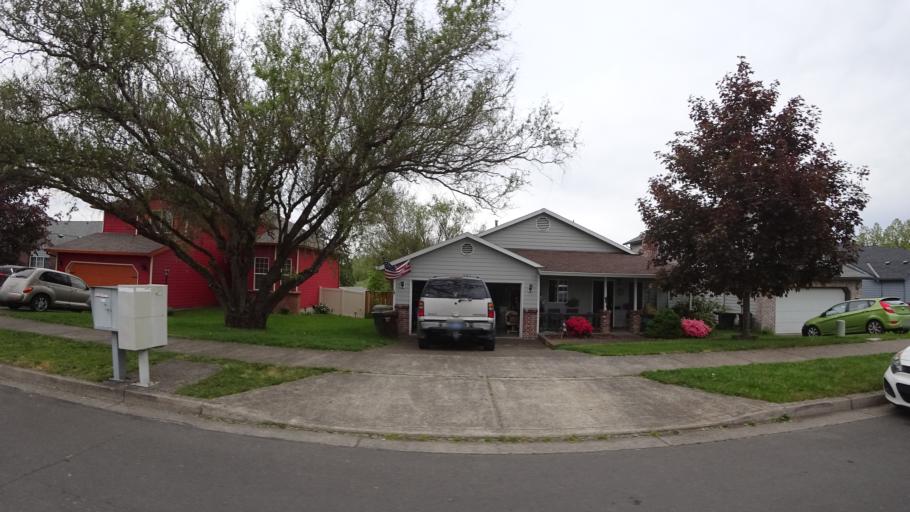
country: US
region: Oregon
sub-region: Washington County
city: Rockcreek
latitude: 45.5164
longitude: -122.9111
